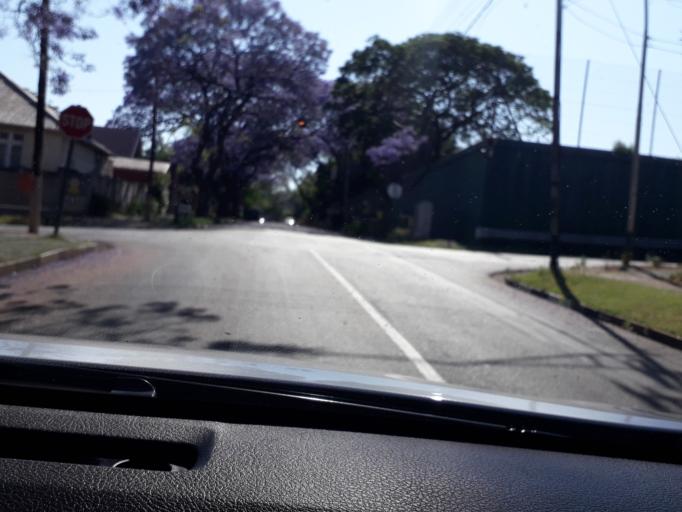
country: ZA
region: Gauteng
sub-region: City of Johannesburg Metropolitan Municipality
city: Johannesburg
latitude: -26.1768
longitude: 28.0030
